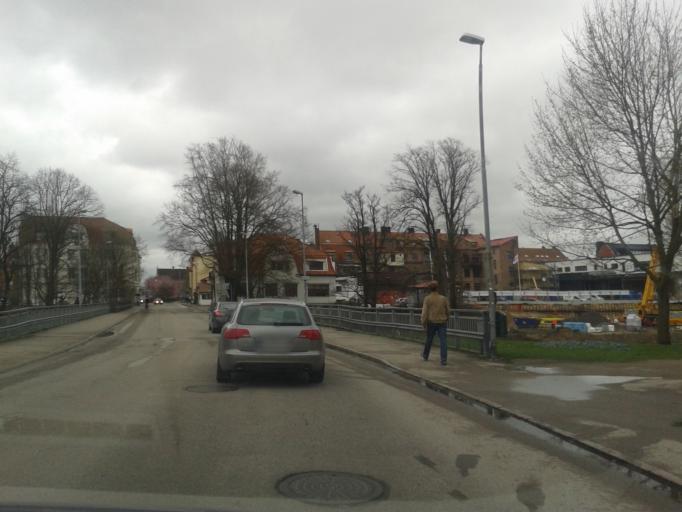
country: SE
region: Skane
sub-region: Angelholms Kommun
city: AEngelholm
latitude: 56.2471
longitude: 12.8618
